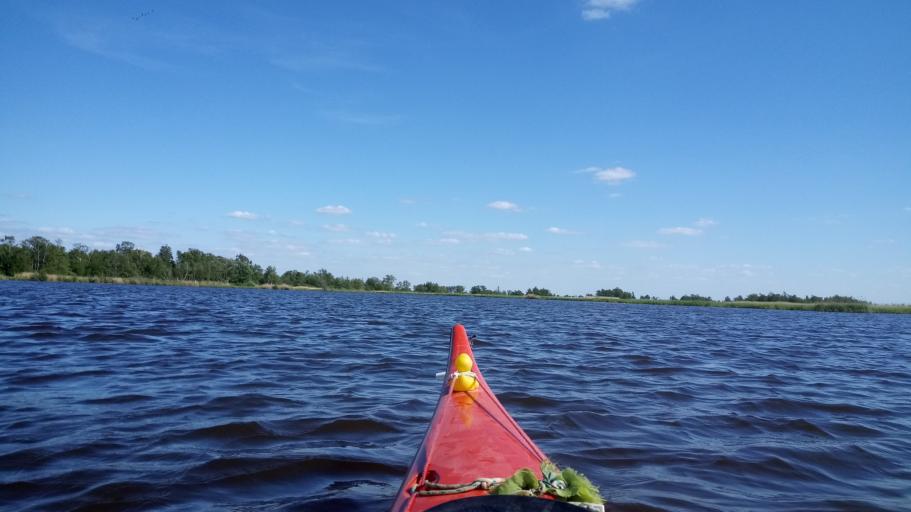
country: NL
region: South Holland
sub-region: Gemeente Nieuwkoop
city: Nieuwkoop
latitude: 52.1549
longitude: 4.8172
